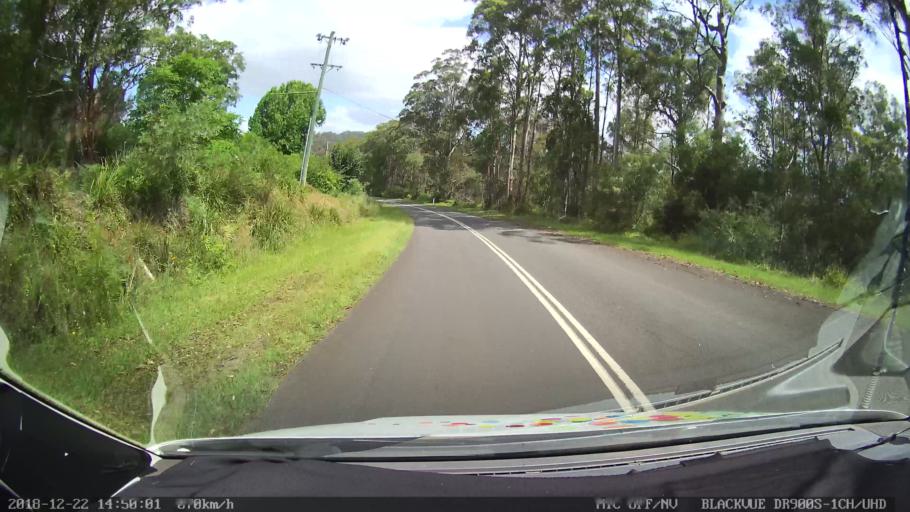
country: AU
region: New South Wales
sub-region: Bellingen
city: Dorrigo
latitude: -30.1919
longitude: 152.5420
